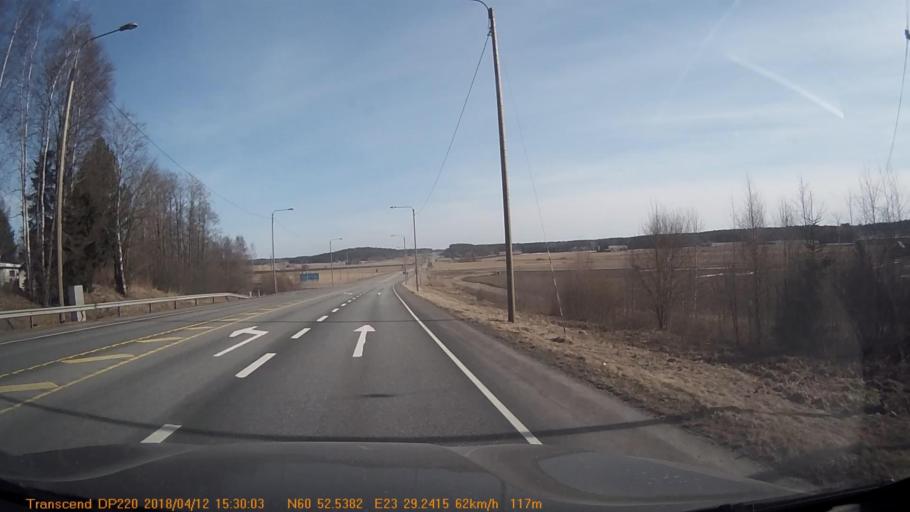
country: FI
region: Haeme
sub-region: Forssa
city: Jokioinen
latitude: 60.8751
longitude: 23.4884
